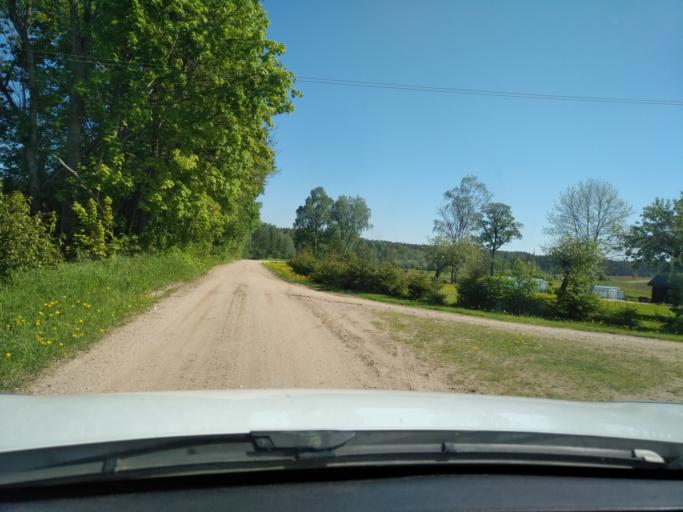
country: LT
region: Panevezys
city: Rokiskis
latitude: 55.7629
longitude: 25.6172
